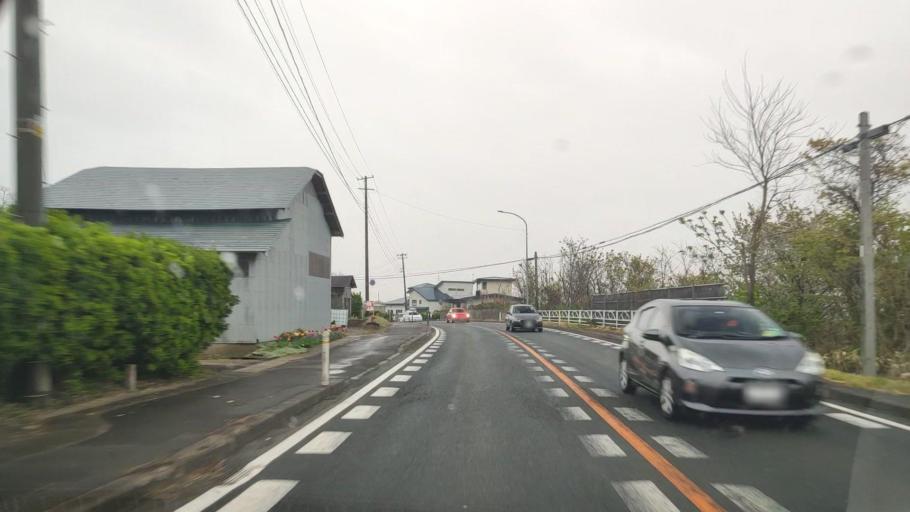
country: JP
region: Akita
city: Noshiromachi
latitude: 40.1111
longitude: 140.0048
